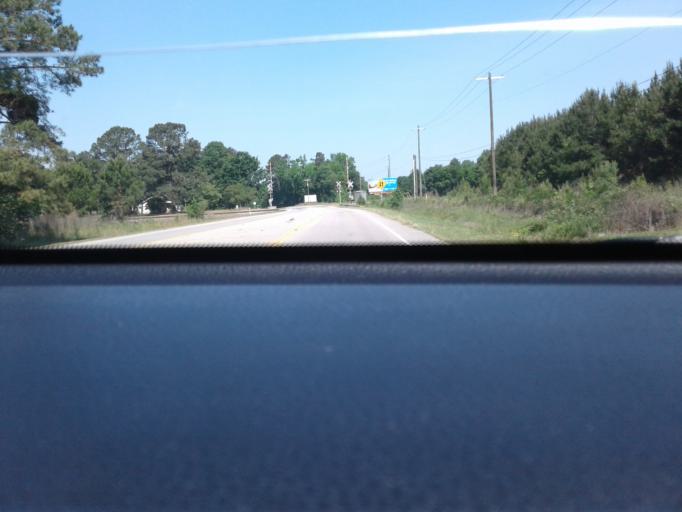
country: US
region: North Carolina
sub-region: Harnett County
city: Lillington
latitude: 35.4257
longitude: -78.8159
